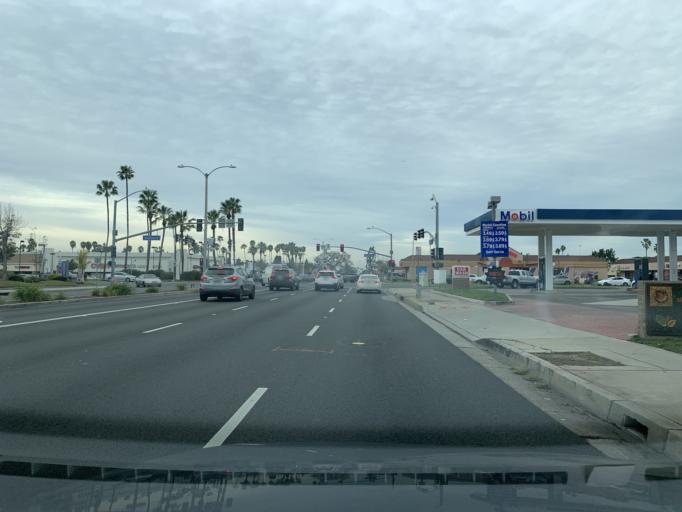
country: US
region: California
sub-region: Orange County
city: Garden Grove
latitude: 33.7887
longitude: -117.9579
